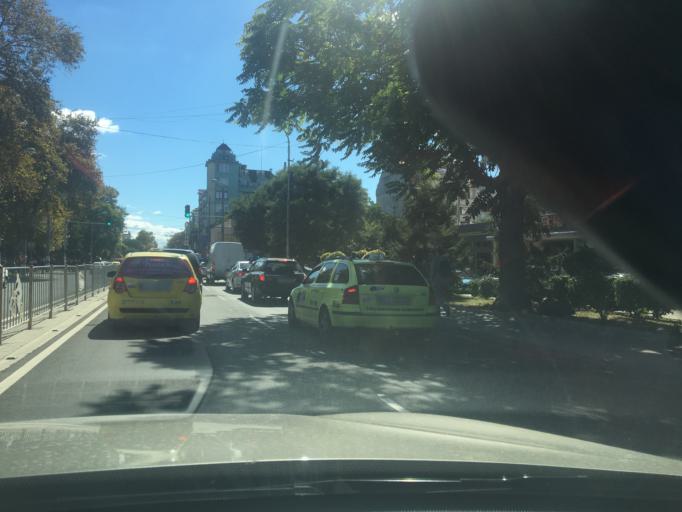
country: BG
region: Burgas
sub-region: Obshtina Burgas
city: Burgas
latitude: 42.5072
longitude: 27.4686
